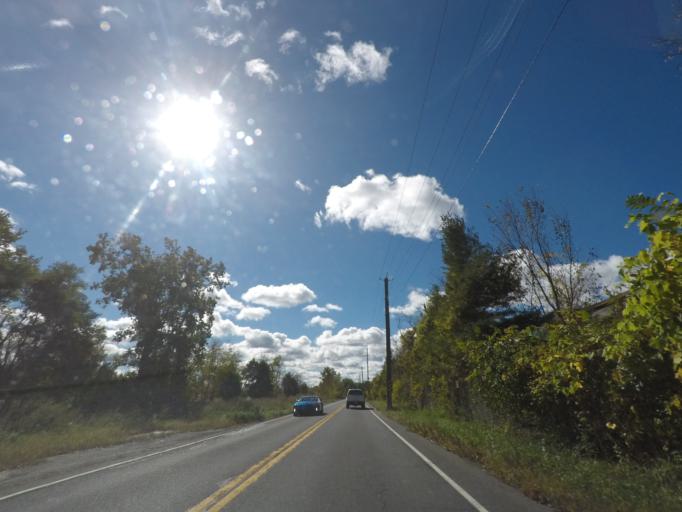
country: US
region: New York
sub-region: Albany County
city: Menands
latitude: 42.7136
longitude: -73.7192
